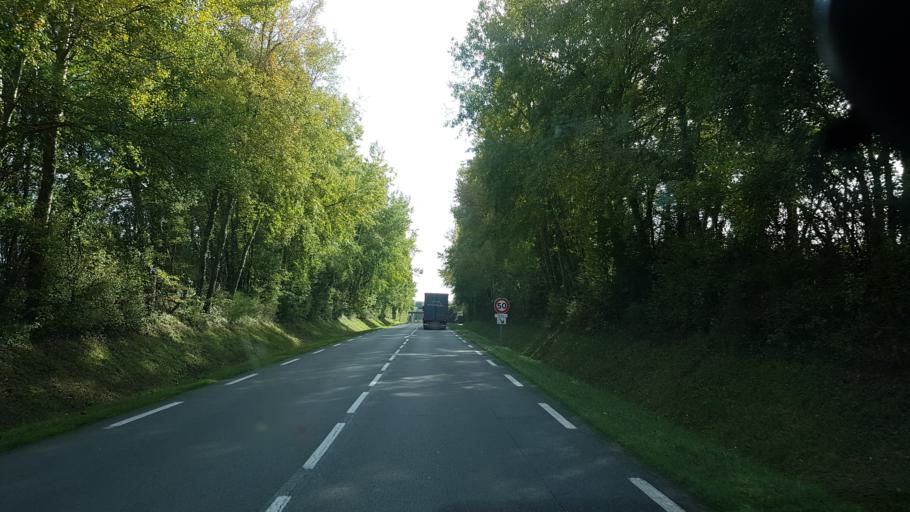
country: FR
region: Poitou-Charentes
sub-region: Departement de la Charente
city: Confolens
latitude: 46.0543
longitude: 0.6666
